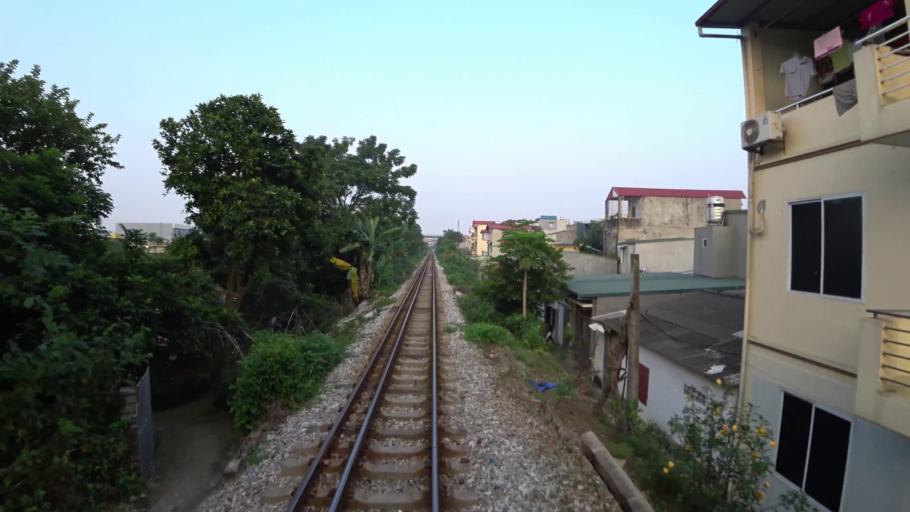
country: VN
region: Ha Noi
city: Trau Quy
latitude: 21.0705
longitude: 105.9016
